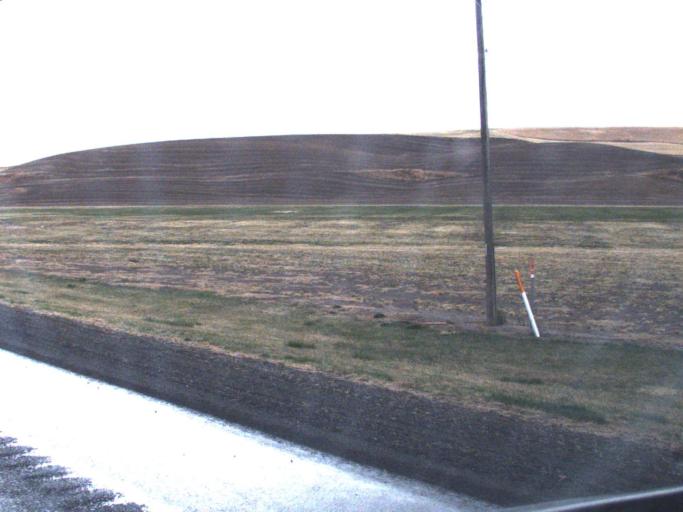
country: US
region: Washington
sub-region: Asotin County
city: Clarkston
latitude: 46.5650
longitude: -117.1143
